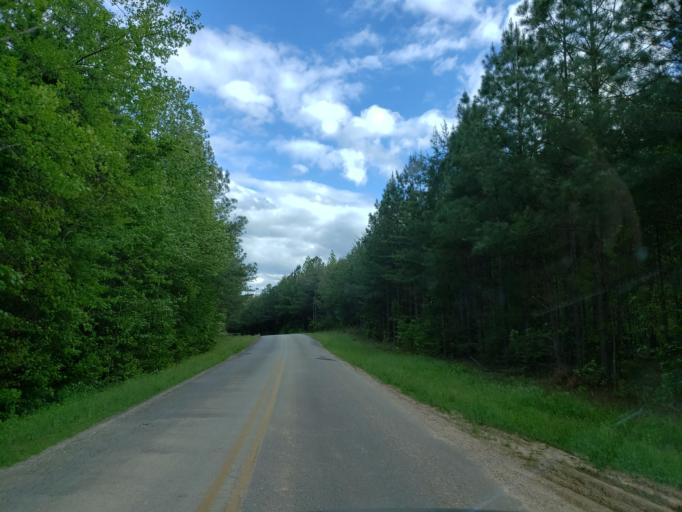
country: US
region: Georgia
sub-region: Haralson County
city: Tallapoosa
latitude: 33.8178
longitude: -85.3703
